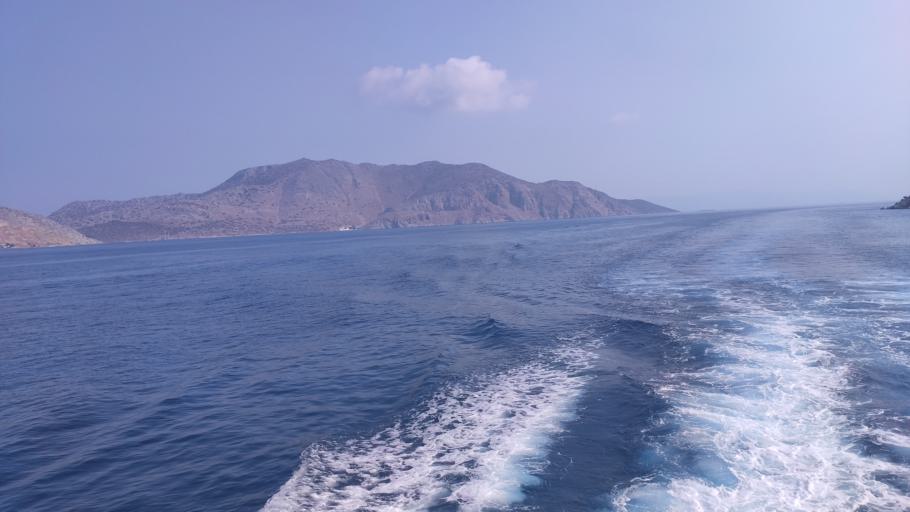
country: GR
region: South Aegean
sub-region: Nomos Dodekanisou
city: Symi
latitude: 36.6216
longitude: 27.8459
